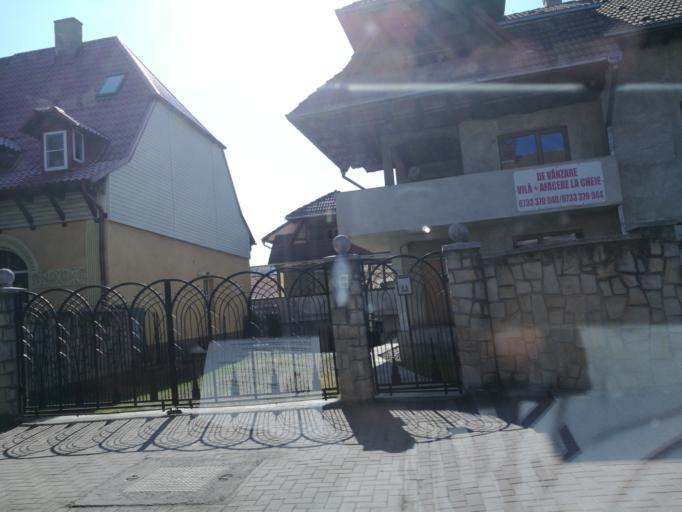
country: RO
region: Suceava
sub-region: Municipiul Suceava
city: Radauti
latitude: 47.8408
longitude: 25.9243
